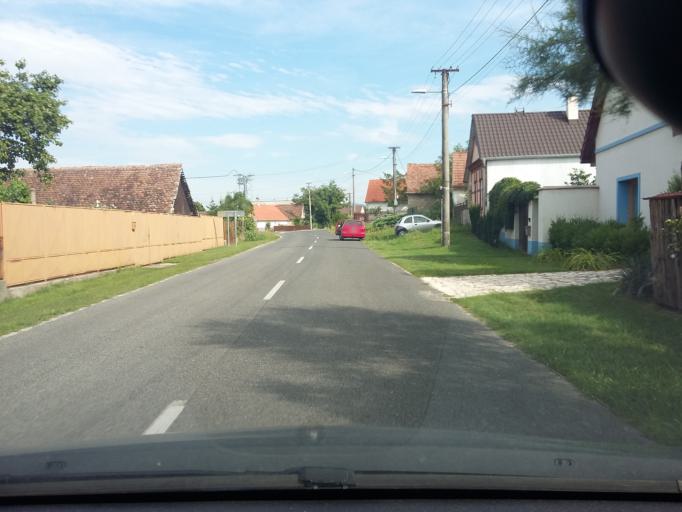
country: SK
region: Trnavsky
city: Gbely
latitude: 48.5722
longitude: 17.2122
